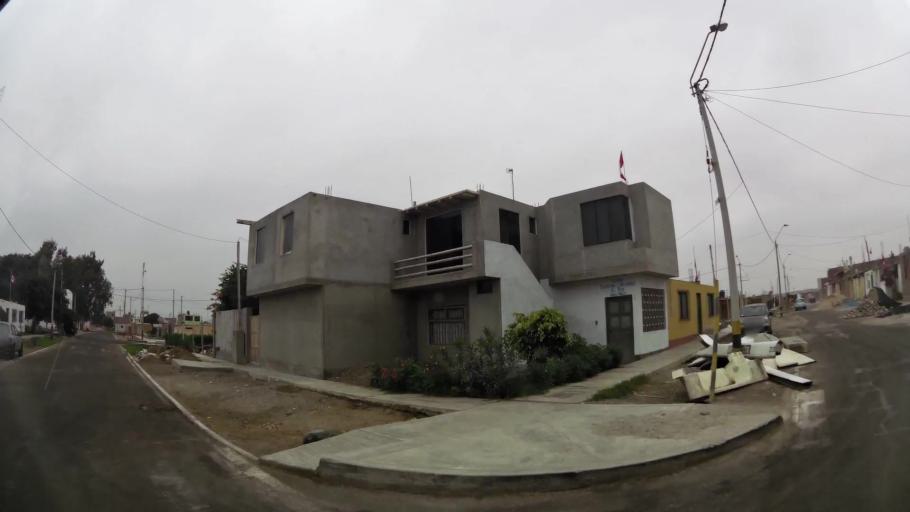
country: PE
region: Ica
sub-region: Provincia de Pisco
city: Paracas
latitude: -13.8382
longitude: -76.2504
